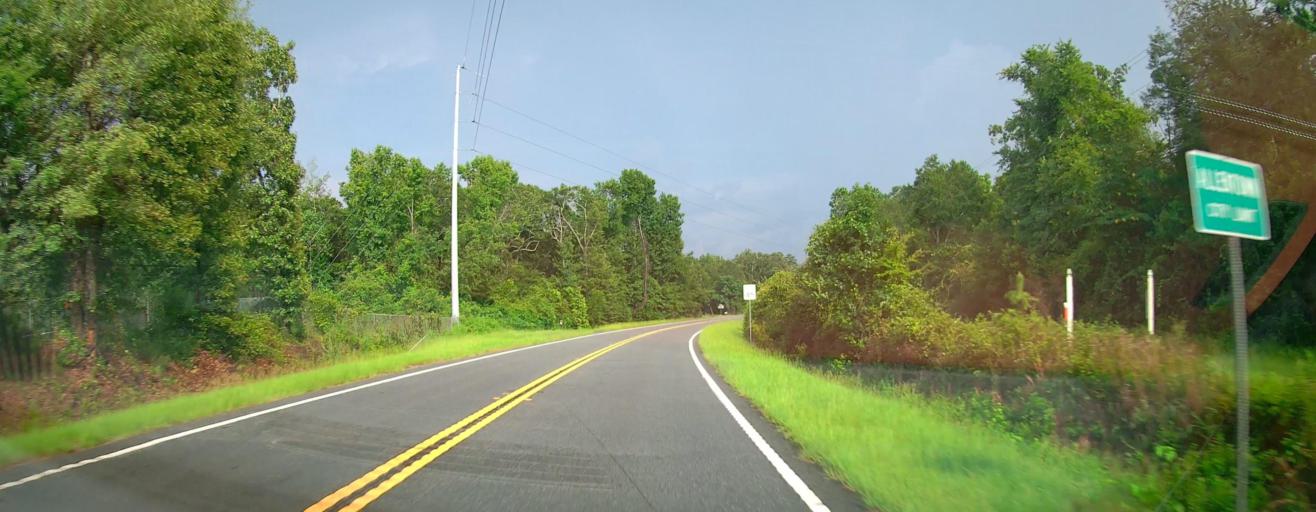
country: US
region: Georgia
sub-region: Twiggs County
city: Jeffersonville
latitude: 32.6006
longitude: -83.2396
